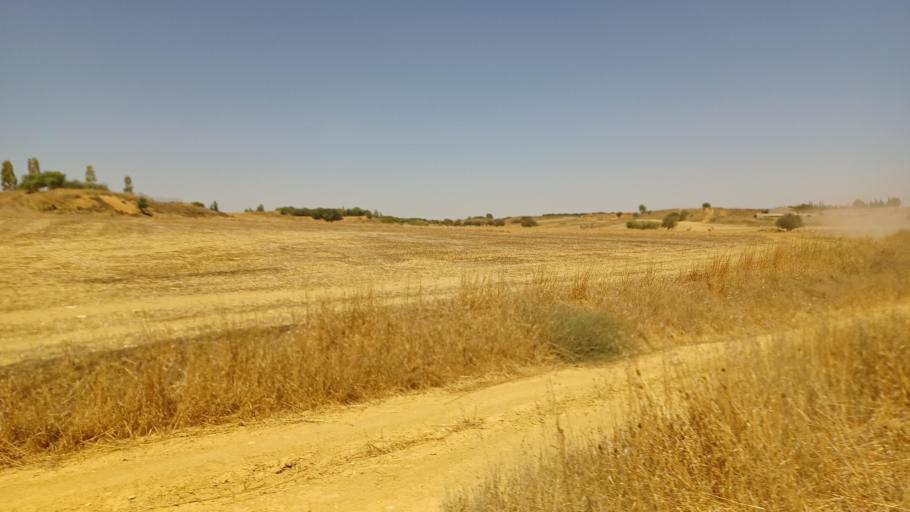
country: CY
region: Ammochostos
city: Avgorou
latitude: 35.0535
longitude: 33.8319
